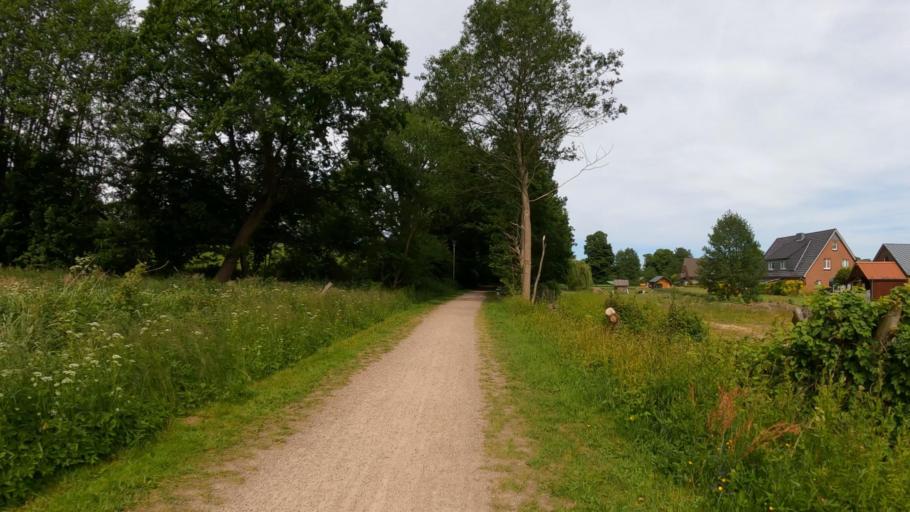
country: DE
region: Schleswig-Holstein
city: Nahe
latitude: 53.7898
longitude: 10.0884
